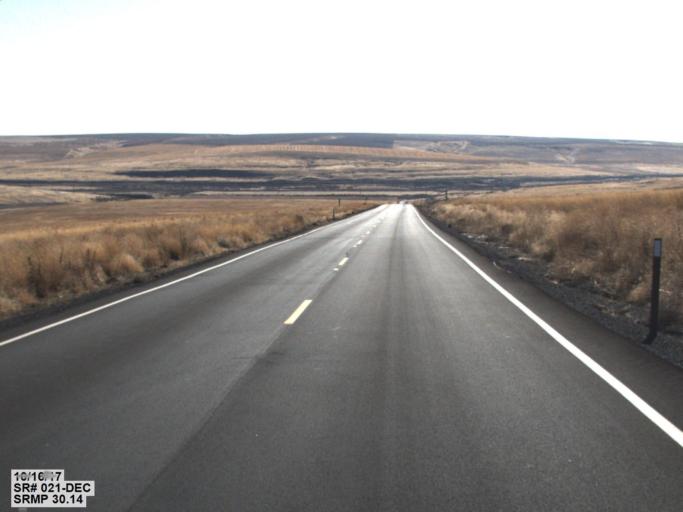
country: US
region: Washington
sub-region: Adams County
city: Ritzville
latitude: 46.9867
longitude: -118.6636
